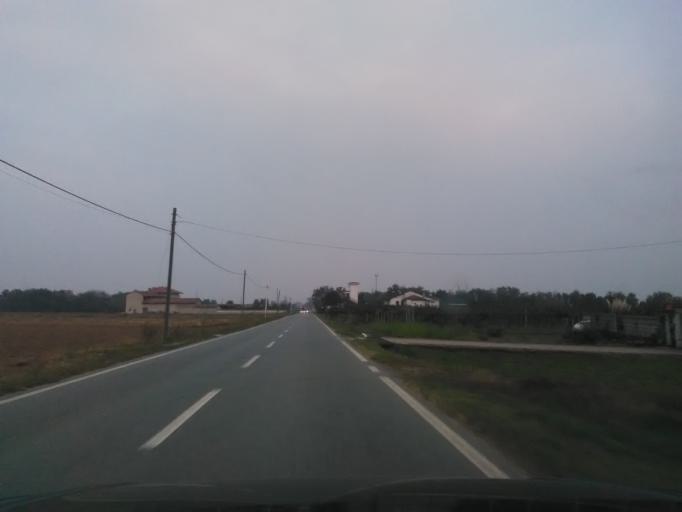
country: IT
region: Piedmont
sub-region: Provincia di Vercelli
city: Alice Castello
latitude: 45.3627
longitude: 8.1076
